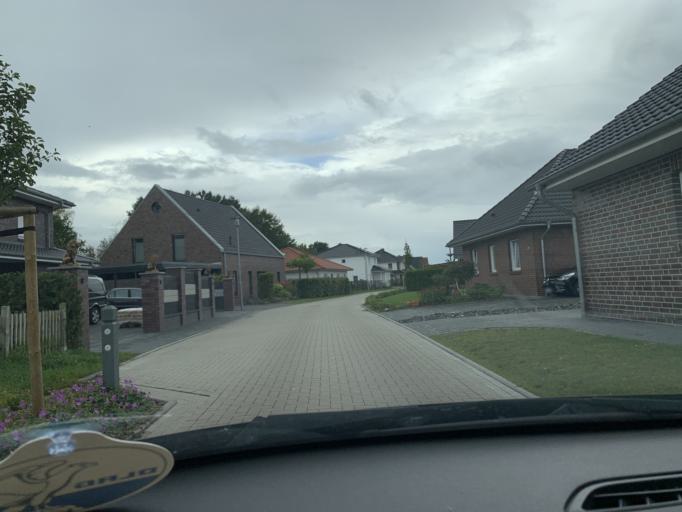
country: DE
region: Lower Saxony
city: Apen
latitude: 53.2280
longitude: 7.7754
